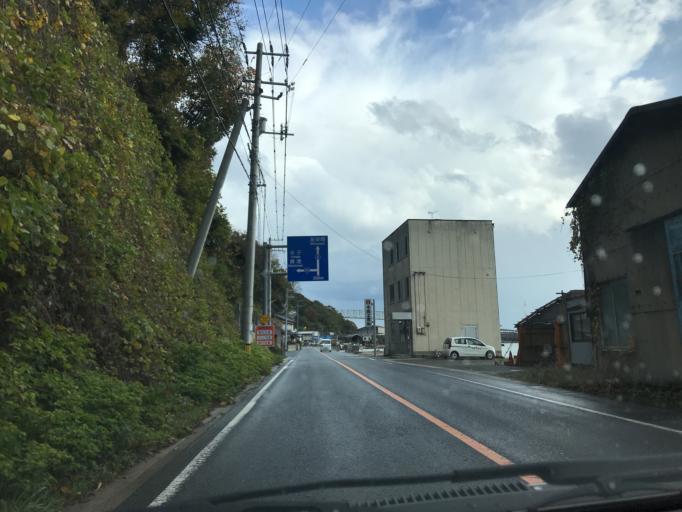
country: JP
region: Shimane
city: Sakaiminato
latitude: 35.5514
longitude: 133.2339
